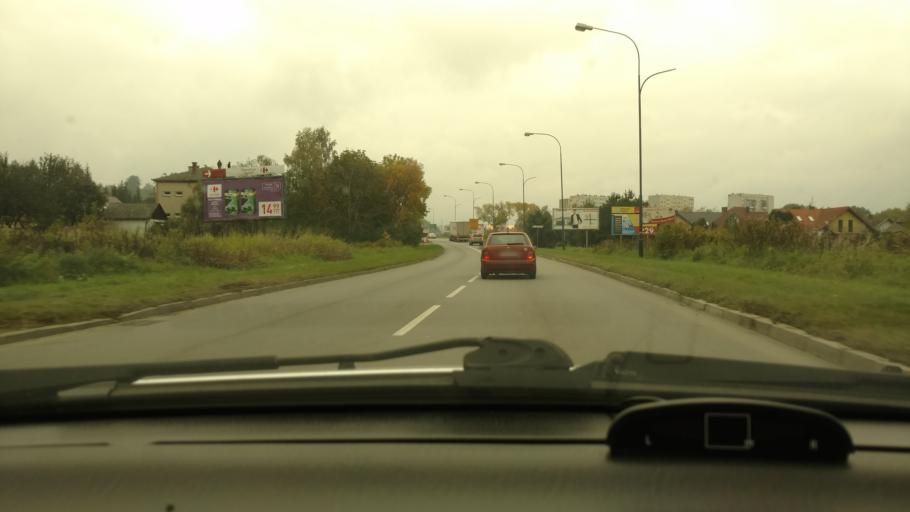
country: PL
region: Lesser Poland Voivodeship
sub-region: Powiat nowosadecki
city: Nowy Sacz
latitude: 49.6342
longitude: 20.7082
